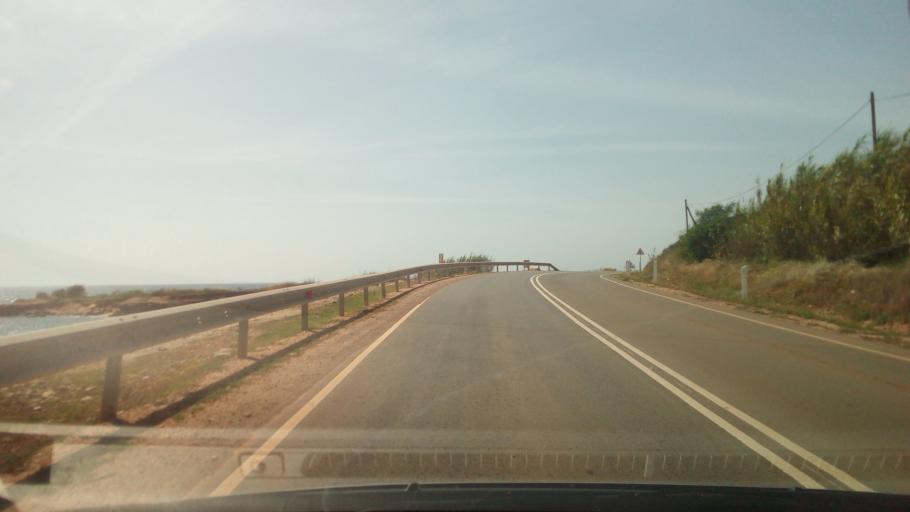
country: CY
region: Larnaka
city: Xylotymbou
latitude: 34.9805
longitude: 33.7729
